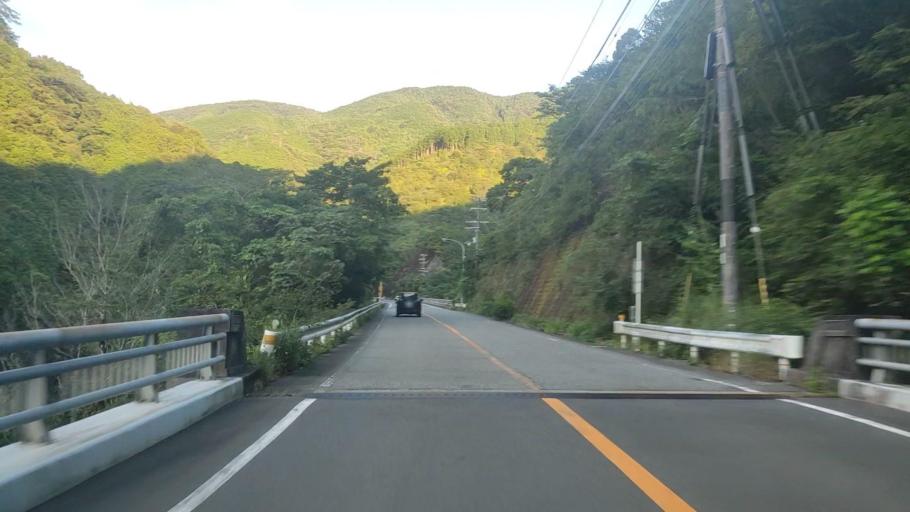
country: JP
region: Wakayama
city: Tanabe
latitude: 33.8142
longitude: 135.5620
